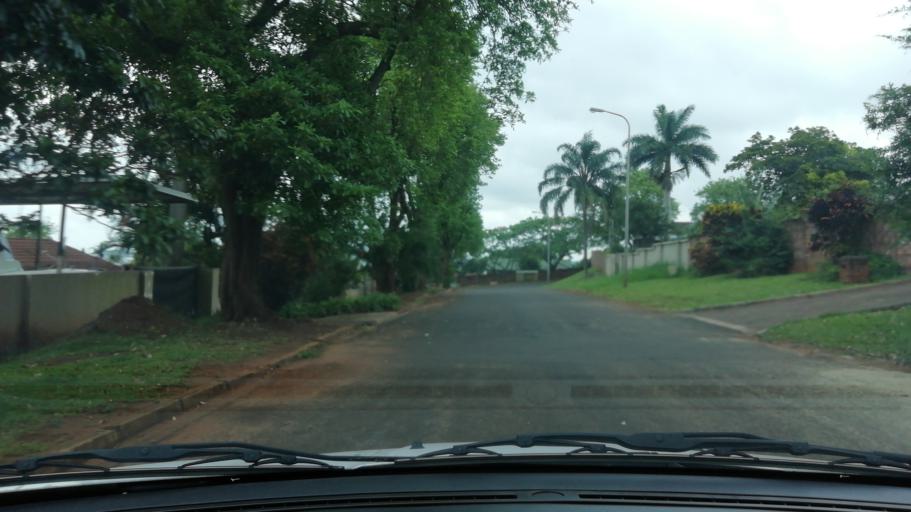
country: ZA
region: KwaZulu-Natal
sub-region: uThungulu District Municipality
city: Empangeni
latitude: -28.7678
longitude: 31.8928
